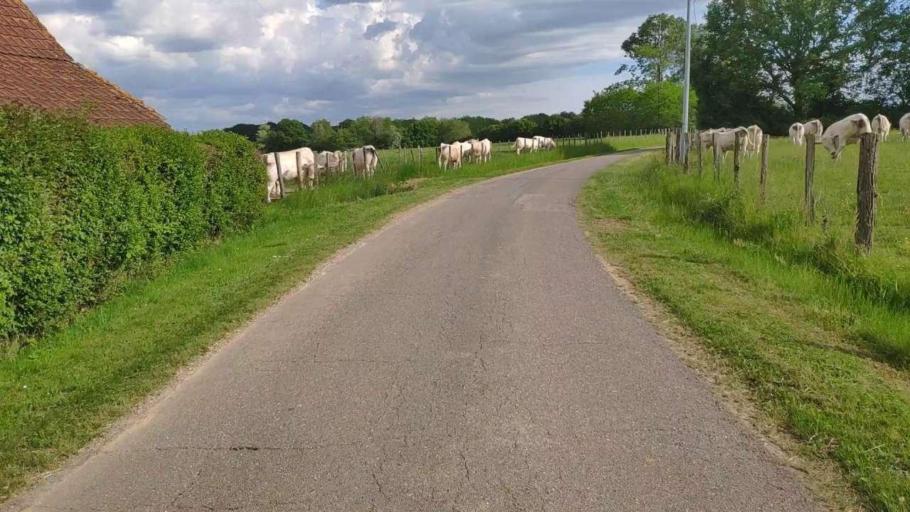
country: FR
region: Bourgogne
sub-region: Departement de Saone-et-Loire
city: Saint-Germain-du-Bois
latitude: 46.7971
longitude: 5.3332
